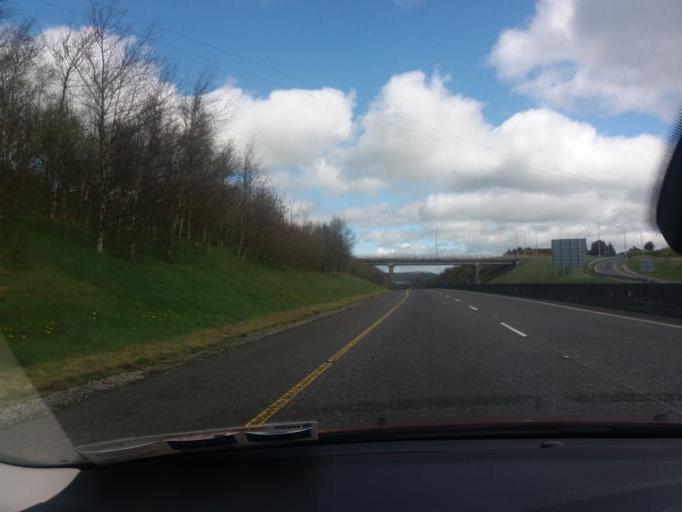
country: IE
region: Munster
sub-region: County Cork
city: Rathcormac
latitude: 52.0529
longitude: -8.3066
